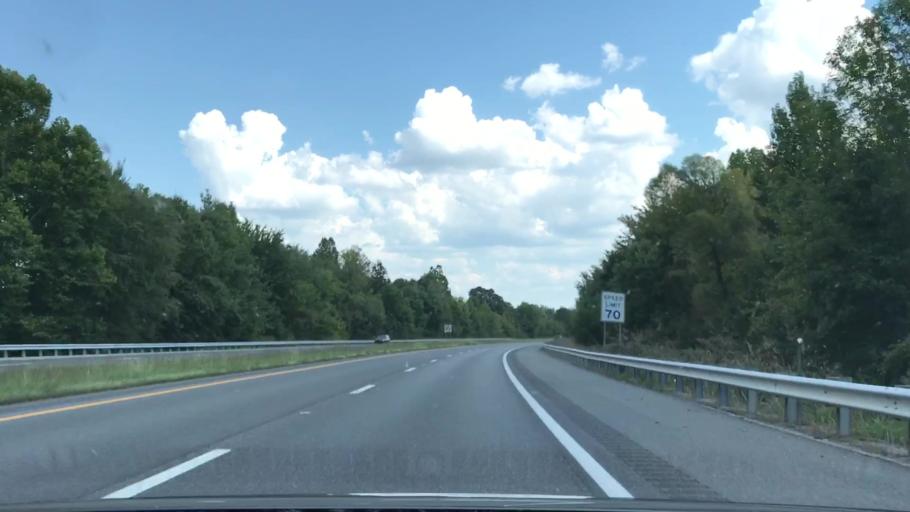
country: US
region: Kentucky
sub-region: Lyon County
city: Eddyville
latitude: 37.1094
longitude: -88.0252
